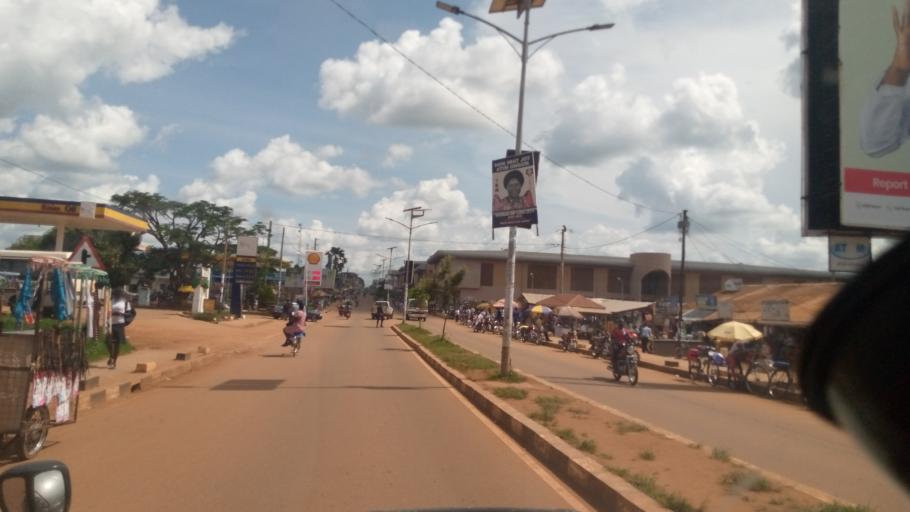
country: UG
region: Northern Region
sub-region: Lira District
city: Lira
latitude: 2.2454
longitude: 32.8987
